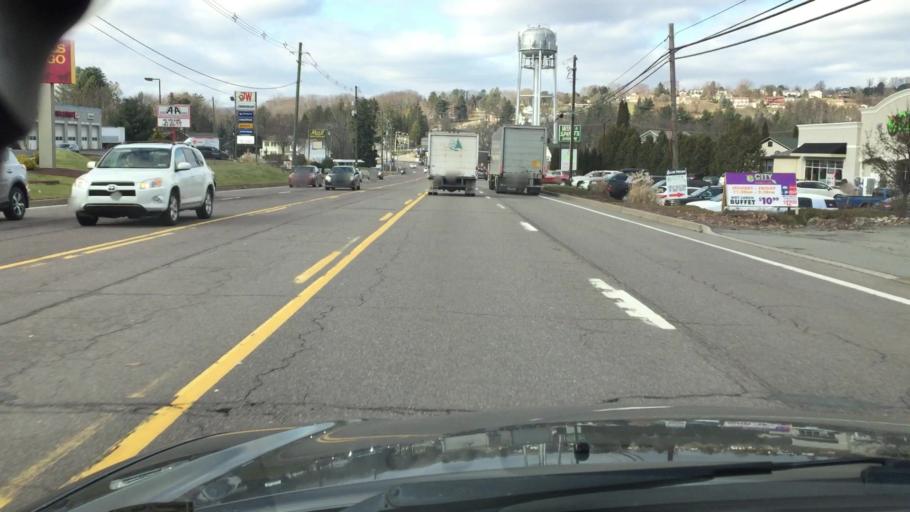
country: US
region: Pennsylvania
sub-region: Luzerne County
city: Shavertown
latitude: 41.3272
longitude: -75.9464
